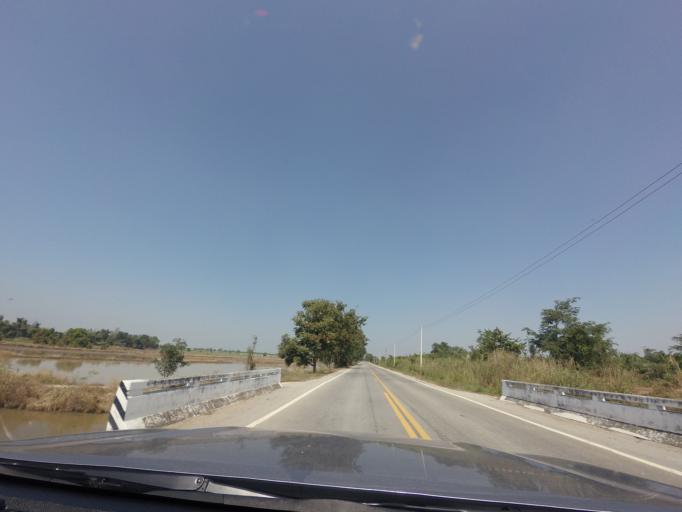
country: TH
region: Sukhothai
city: Sukhothai
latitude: 17.0827
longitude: 99.7907
